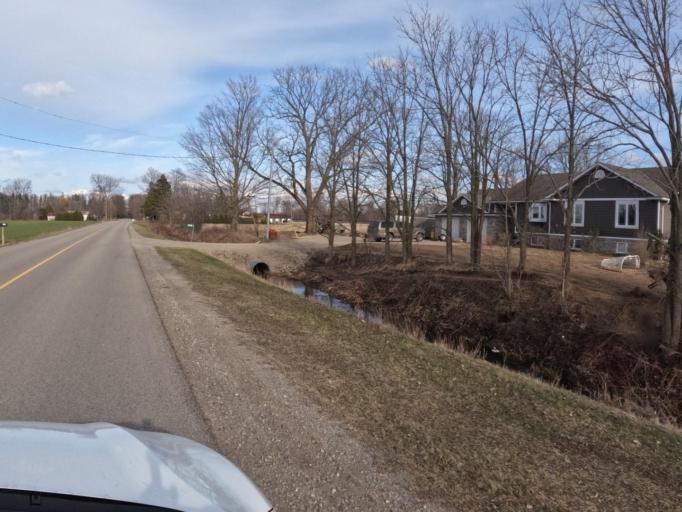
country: CA
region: Ontario
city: Brant
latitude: 43.0014
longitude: -80.4386
